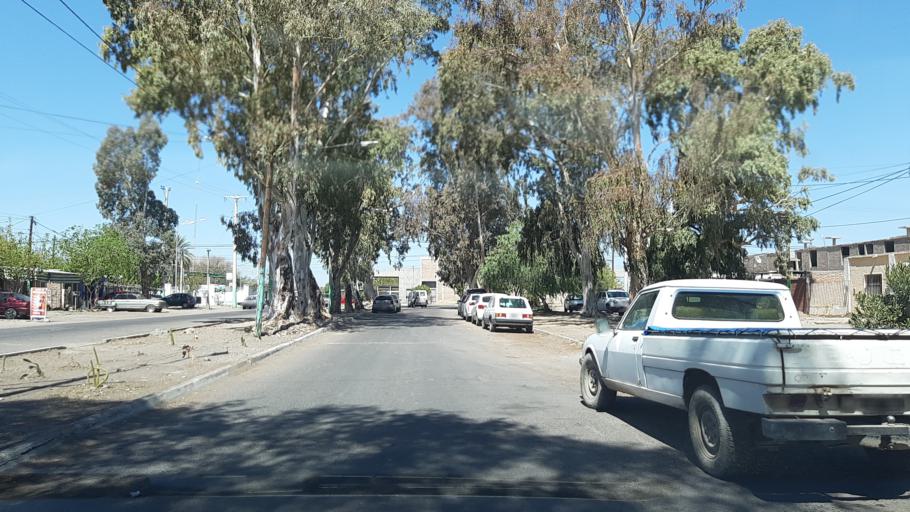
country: AR
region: San Juan
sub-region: Departamento de Rivadavia
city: Rivadavia
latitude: -31.5233
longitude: -68.6247
